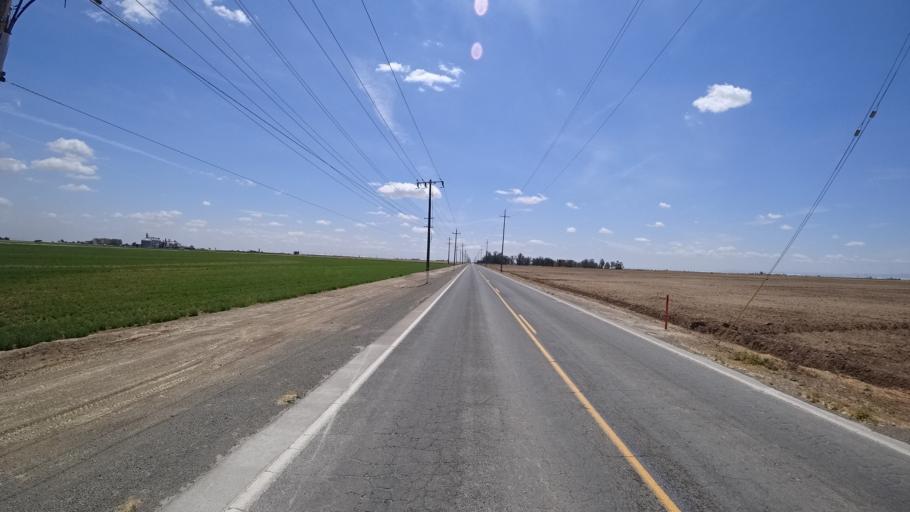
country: US
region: California
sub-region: Kings County
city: Home Garden
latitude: 36.2254
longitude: -119.6549
